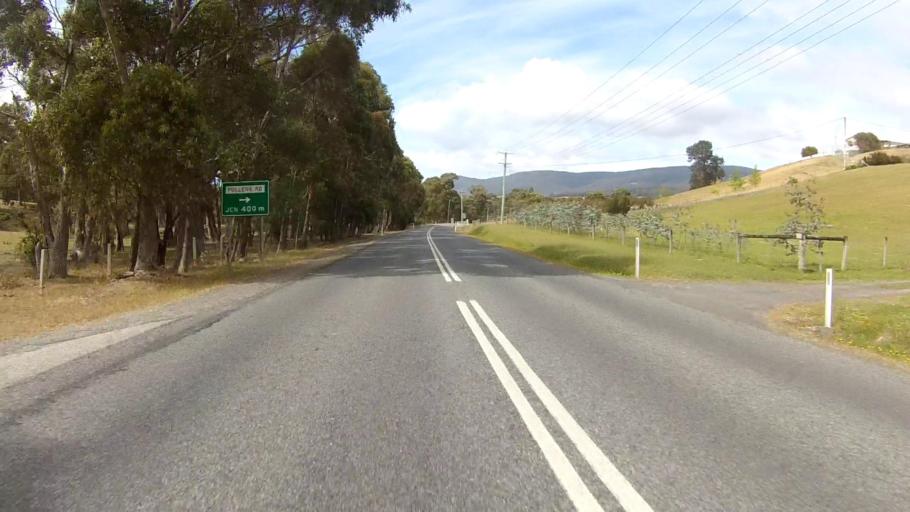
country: AU
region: Tasmania
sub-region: Kingborough
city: Kettering
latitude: -43.1496
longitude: 147.2399
